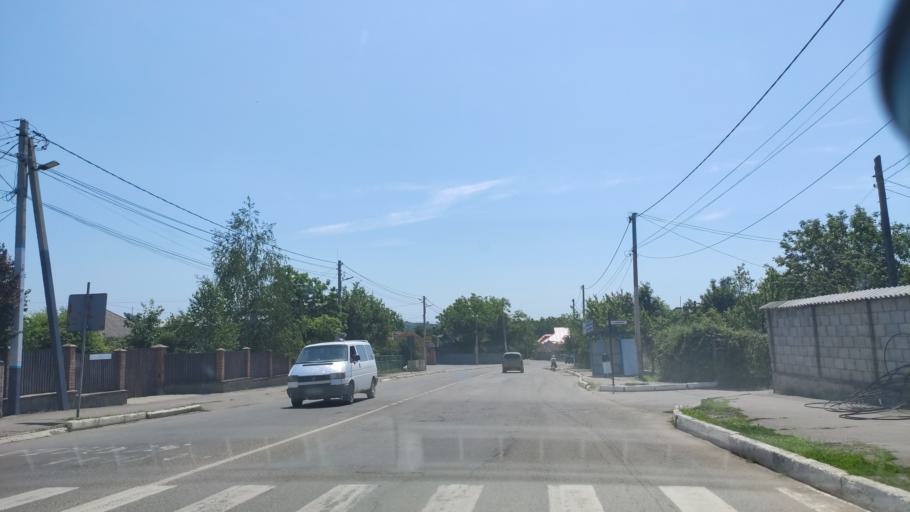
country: MD
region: Raionul Soroca
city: Soroca
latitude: 48.1667
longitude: 28.3036
